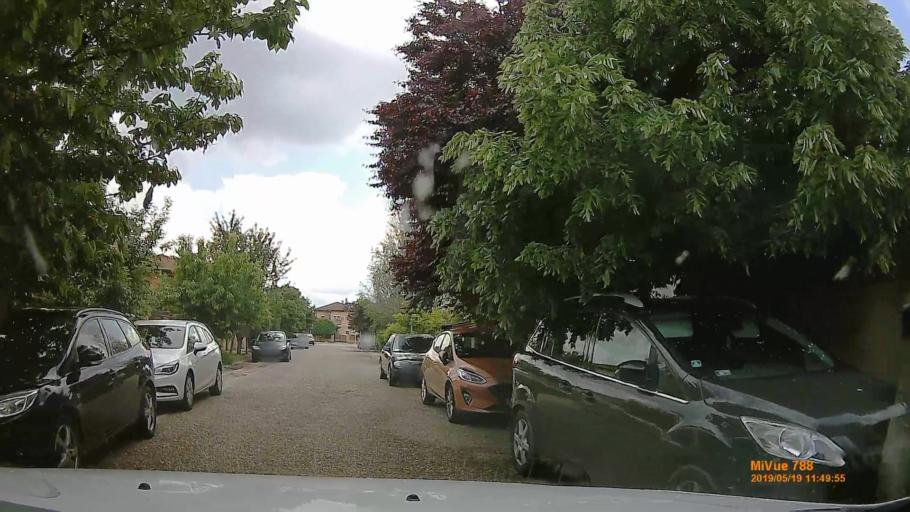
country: HU
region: Budapest
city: Budapest XVII. keruelet
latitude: 47.4685
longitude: 19.2251
